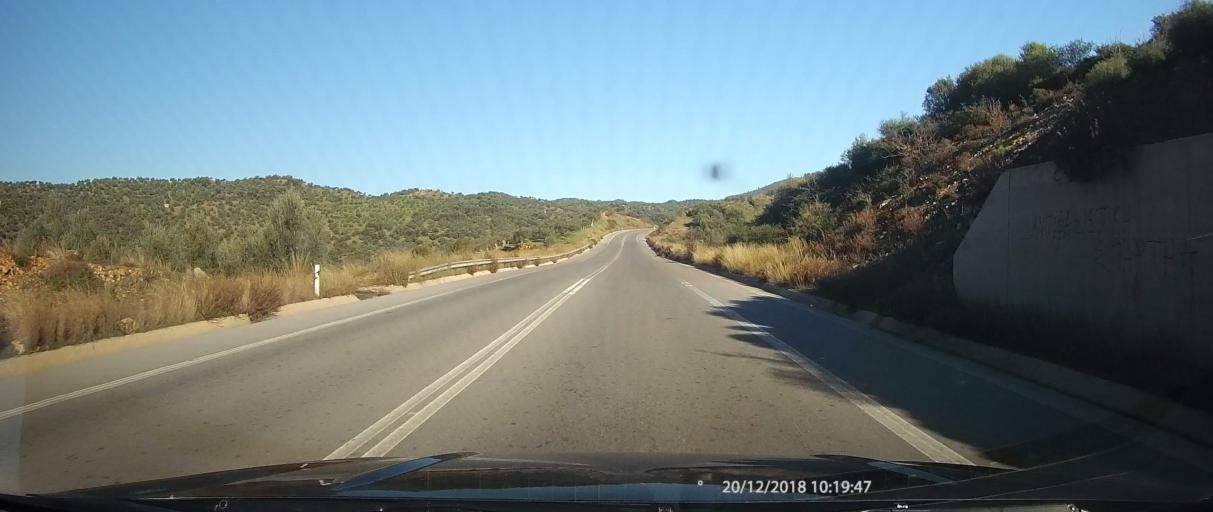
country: GR
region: Peloponnese
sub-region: Nomos Lakonias
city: Magoula
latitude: 37.1396
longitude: 22.4248
